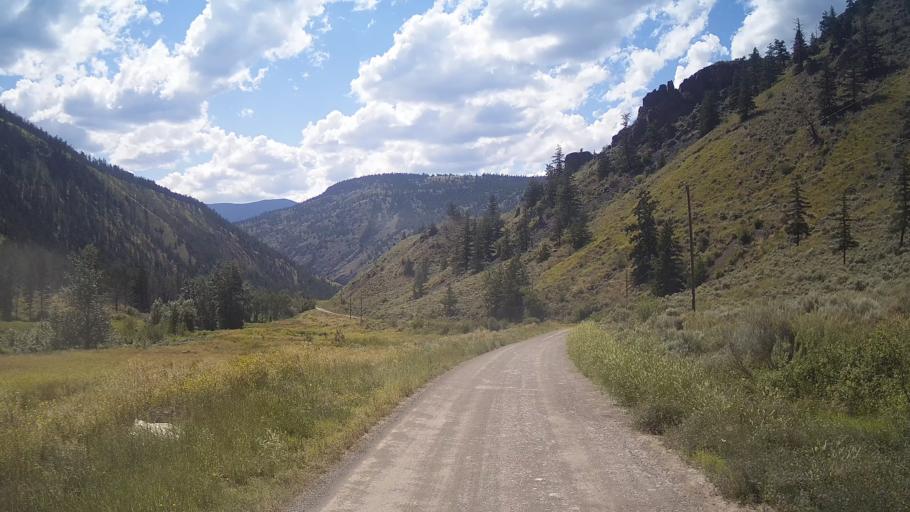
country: CA
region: British Columbia
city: Lillooet
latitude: 51.2251
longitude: -122.0676
